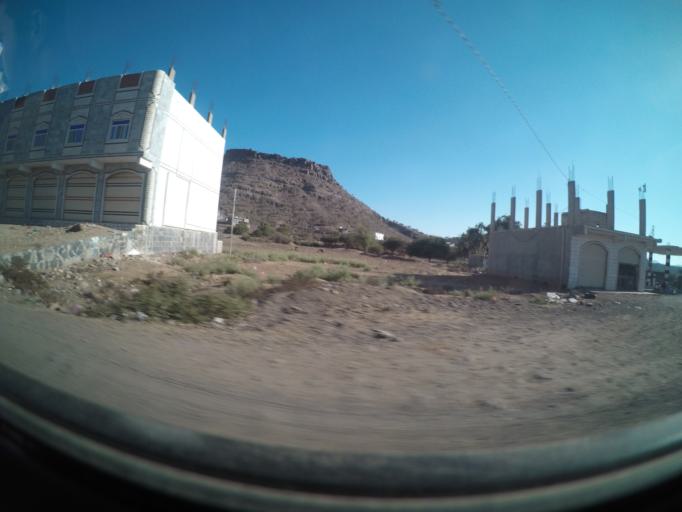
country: YE
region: Ad Dali'
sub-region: Ad Dhale'e
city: Dhalie
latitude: 13.6729
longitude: 44.7582
